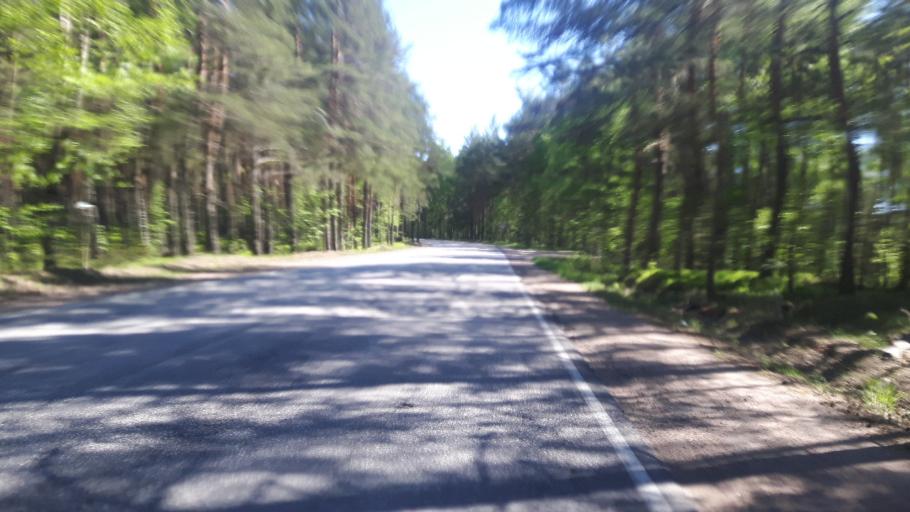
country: RU
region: Leningrad
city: Glebychevo
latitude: 60.2905
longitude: 28.8703
